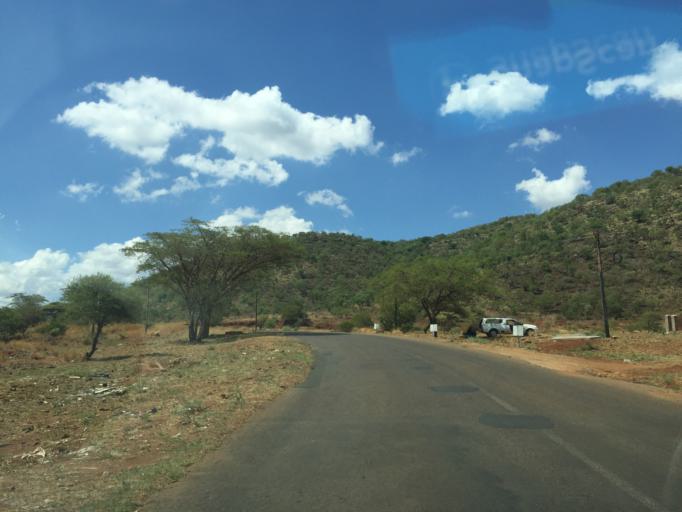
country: ZA
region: North-West
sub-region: Bojanala Platinum District Municipality
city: Mogwase
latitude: -25.3513
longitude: 27.0659
